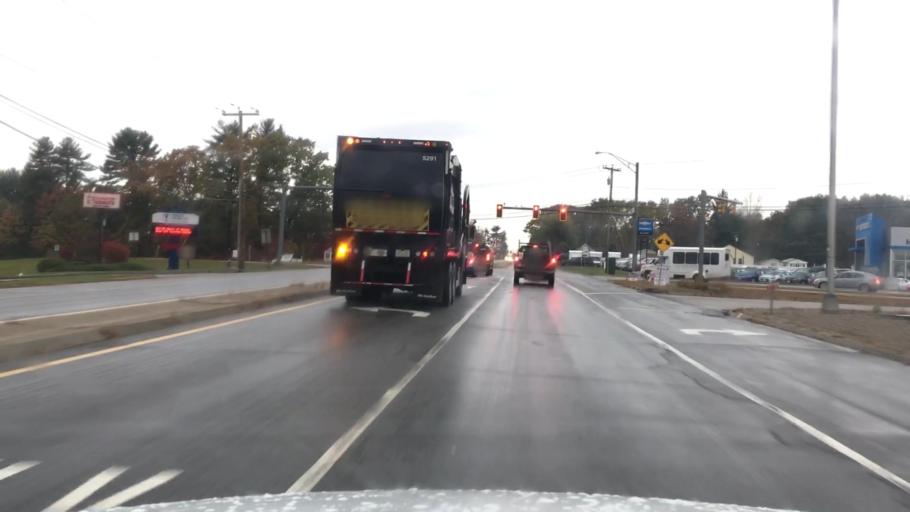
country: US
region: New Hampshire
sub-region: Strafford County
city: Somersworth
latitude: 43.2646
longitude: -70.9061
